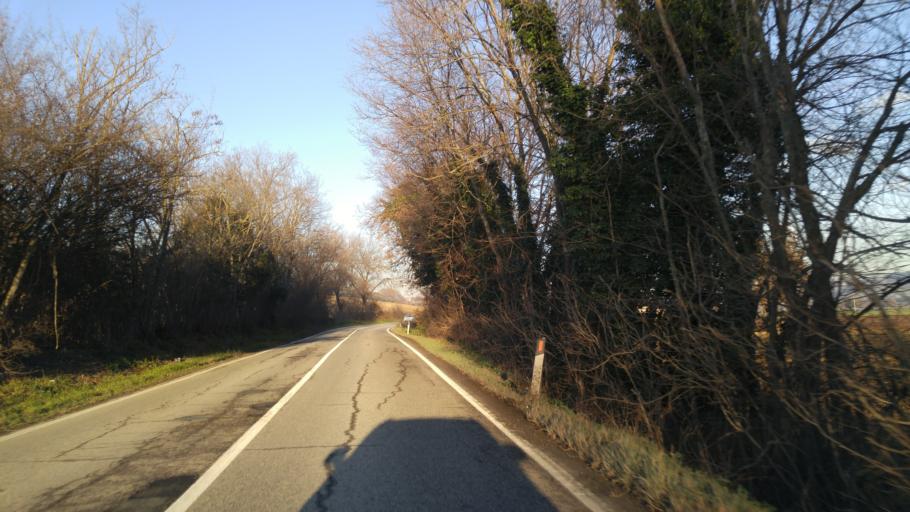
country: IT
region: The Marches
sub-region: Provincia di Pesaro e Urbino
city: Monte Porzio
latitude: 43.6812
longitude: 13.0322
